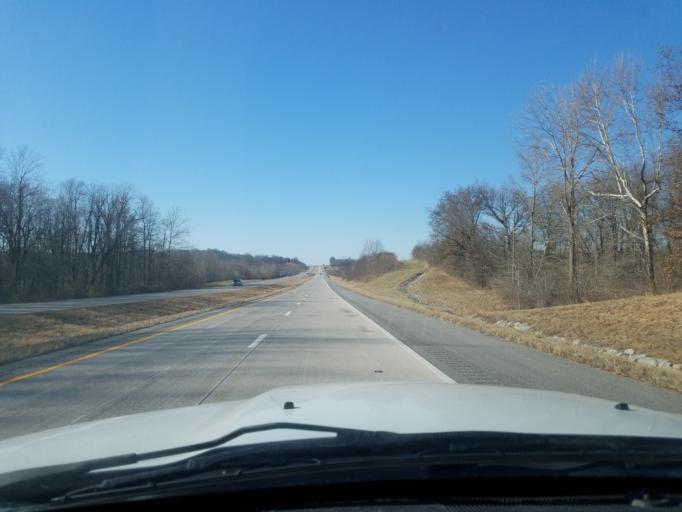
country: US
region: Kentucky
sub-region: Henderson County
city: Henderson
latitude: 37.7790
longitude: -87.4502
